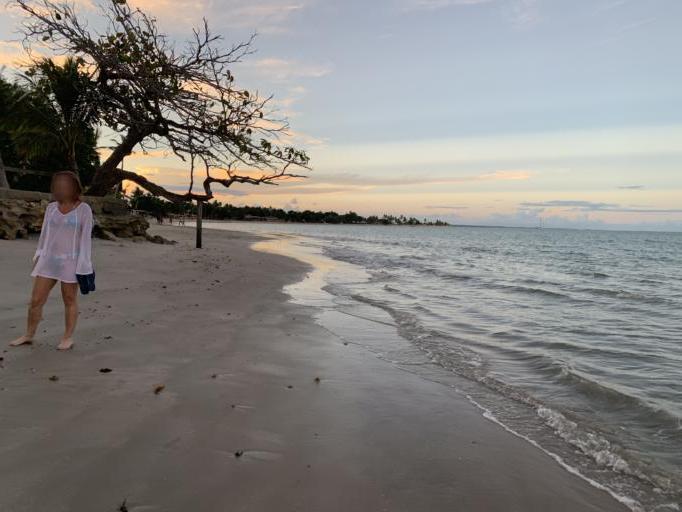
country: BR
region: Bahia
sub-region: Santa Cruz Cabralia
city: Santa Cruz Cabralia
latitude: -16.3413
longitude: -39.0062
